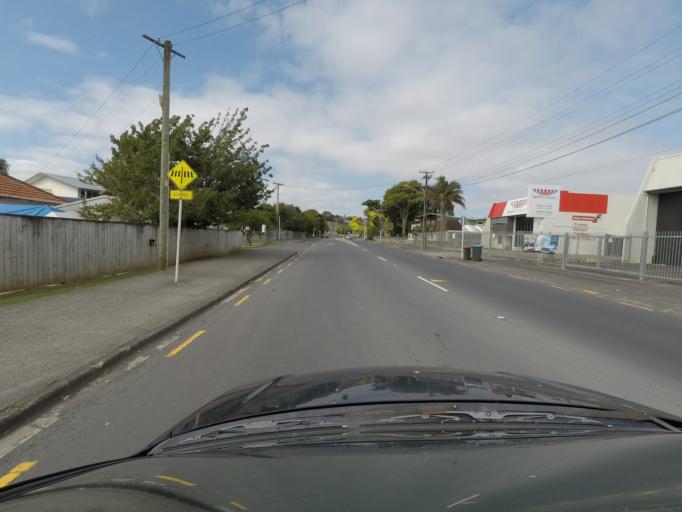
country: NZ
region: Auckland
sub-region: Auckland
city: Auckland
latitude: -36.9130
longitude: 174.7475
